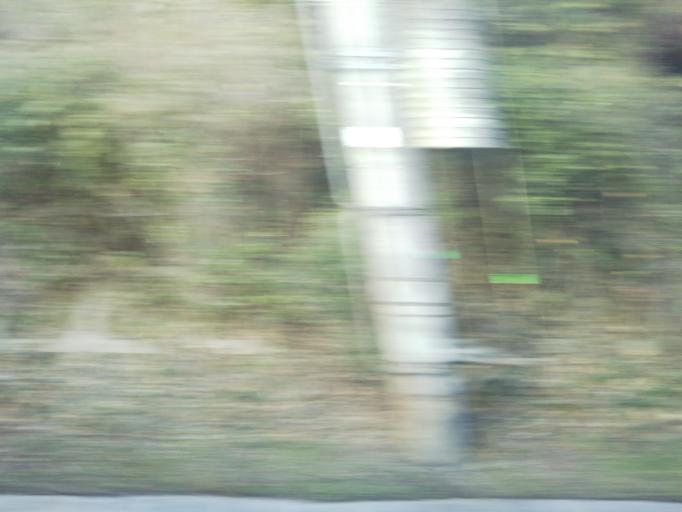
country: JP
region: Kagawa
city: Sakaidecho
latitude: 34.4544
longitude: 133.8071
